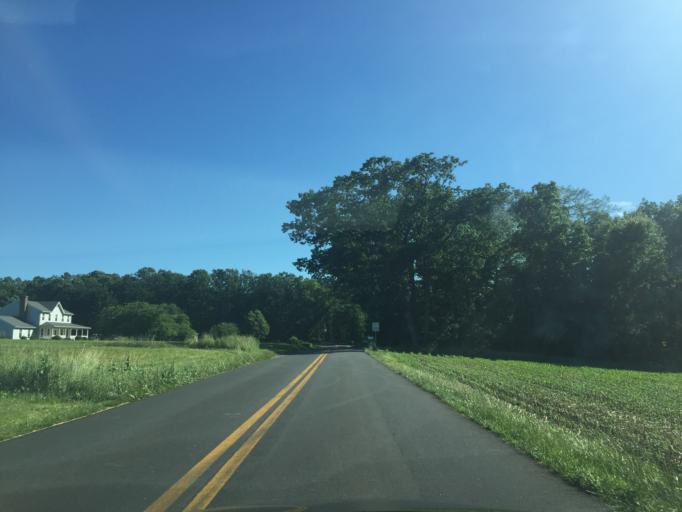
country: US
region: Maryland
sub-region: Carroll County
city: Hampstead
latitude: 39.5734
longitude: -76.9187
